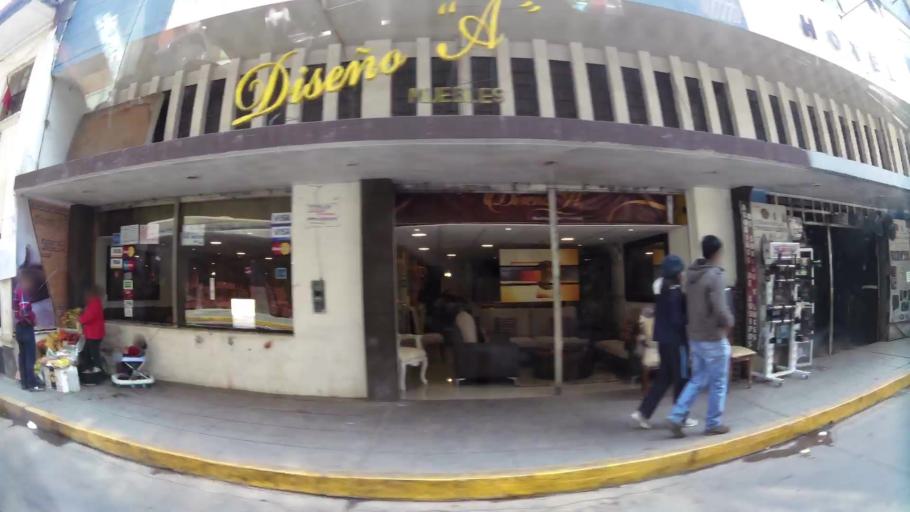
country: PE
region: Junin
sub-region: Provincia de Huancayo
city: Huancayo
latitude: -12.0705
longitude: -75.2100
